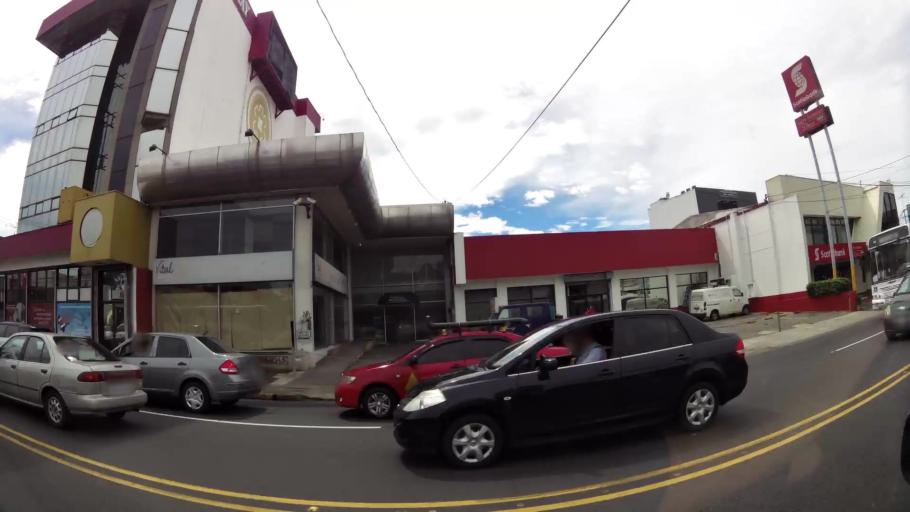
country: CR
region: San Jose
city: San Pedro
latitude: 9.9319
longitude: -84.0489
